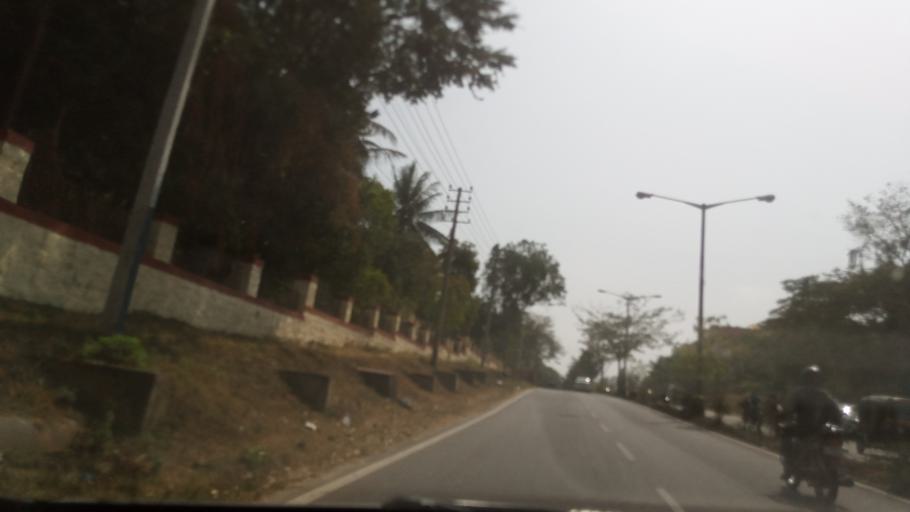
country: IN
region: Karnataka
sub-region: Mysore
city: Mysore
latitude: 12.3297
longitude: 76.6331
